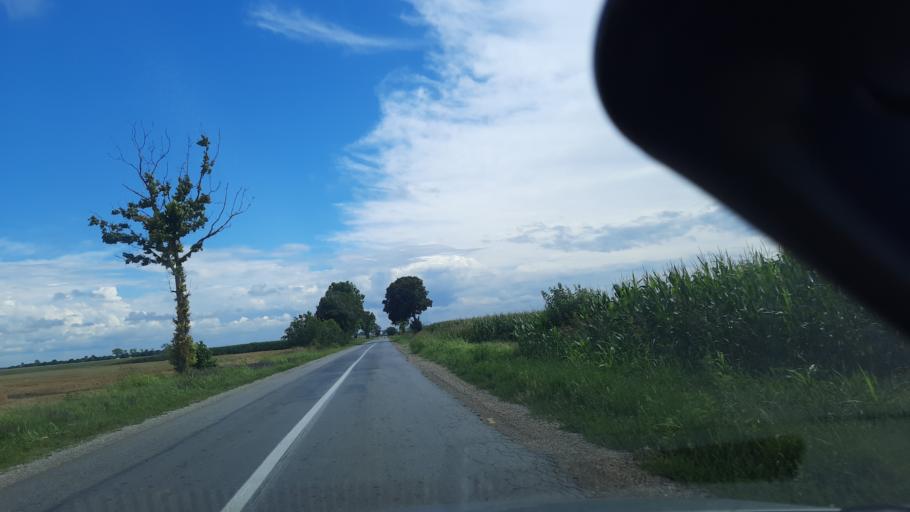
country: RS
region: Autonomna Pokrajina Vojvodina
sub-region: Sremski Okrug
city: Sremska Mitrovica
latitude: 45.0594
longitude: 19.5987
